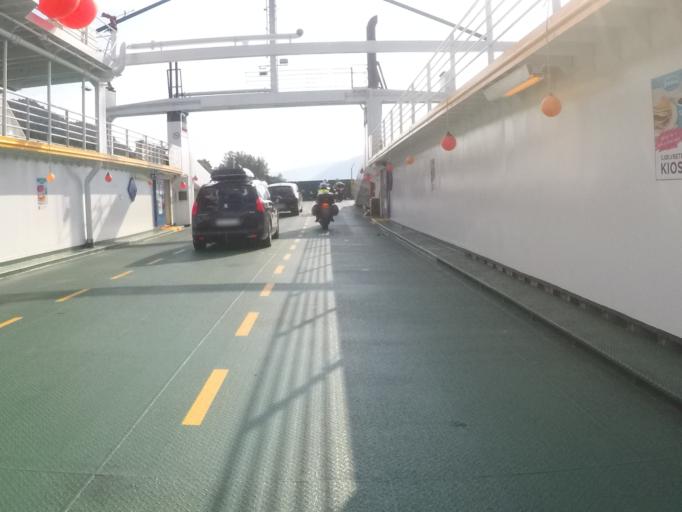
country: NO
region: More og Romsdal
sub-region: Molde
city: Hjelset
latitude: 62.6848
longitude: 7.4655
